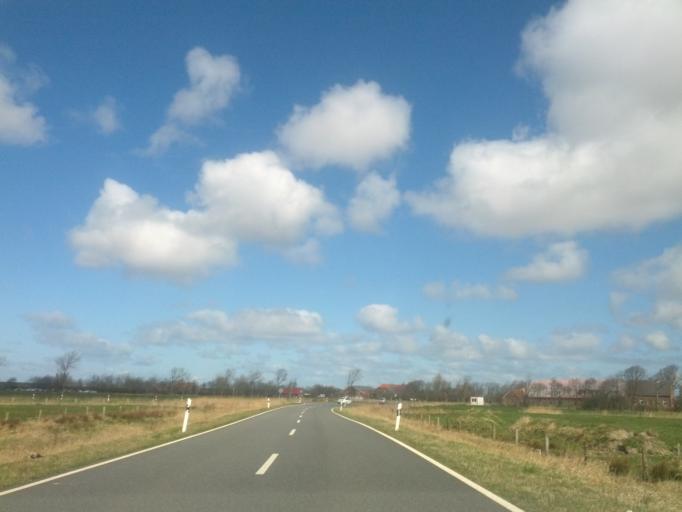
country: DE
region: Lower Saxony
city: Esens
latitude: 53.6724
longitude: 7.5844
